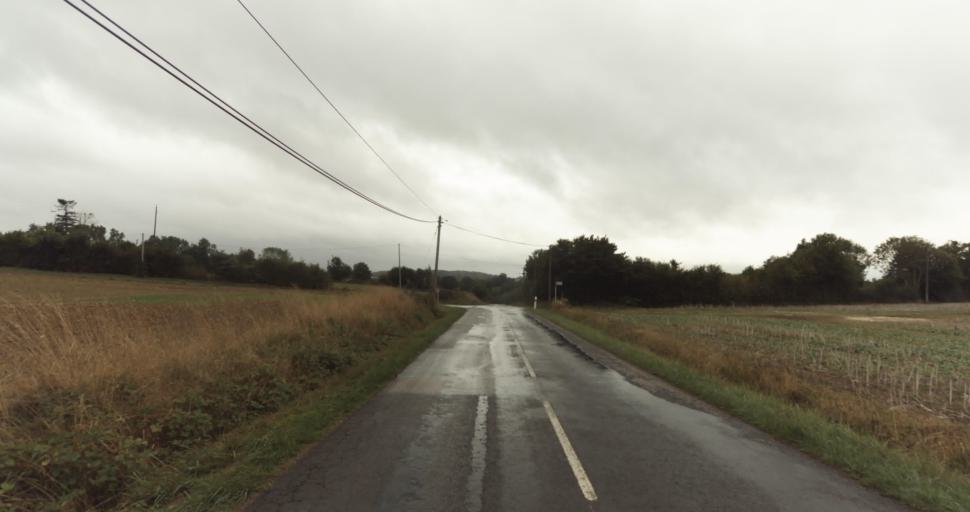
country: FR
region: Lower Normandy
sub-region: Departement de l'Orne
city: Sainte-Gauburge-Sainte-Colombe
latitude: 48.7287
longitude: 0.4337
